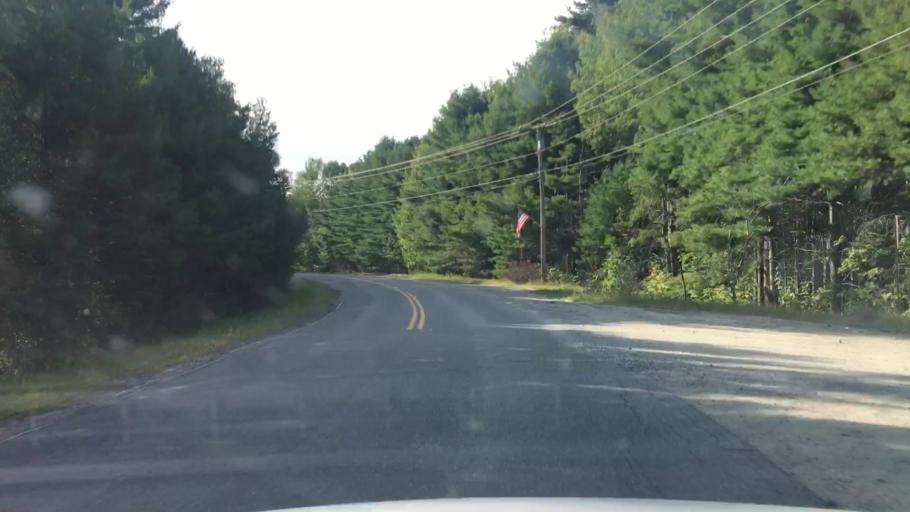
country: US
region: Maine
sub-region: Penobscot County
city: Enfield
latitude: 45.2366
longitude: -68.5455
